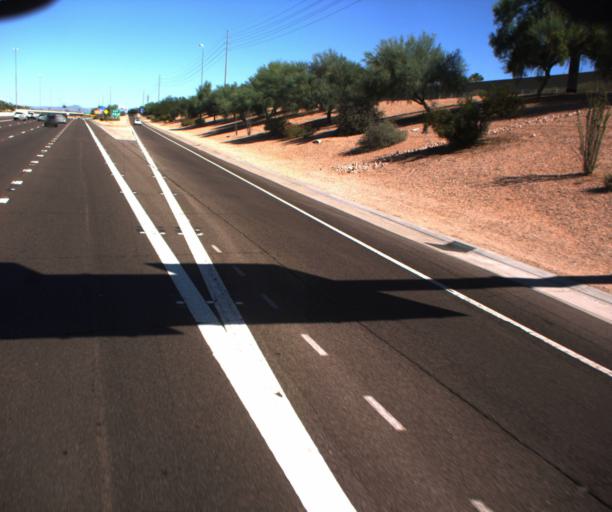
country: US
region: Arizona
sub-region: Maricopa County
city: Paradise Valley
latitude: 33.6123
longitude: -111.8912
